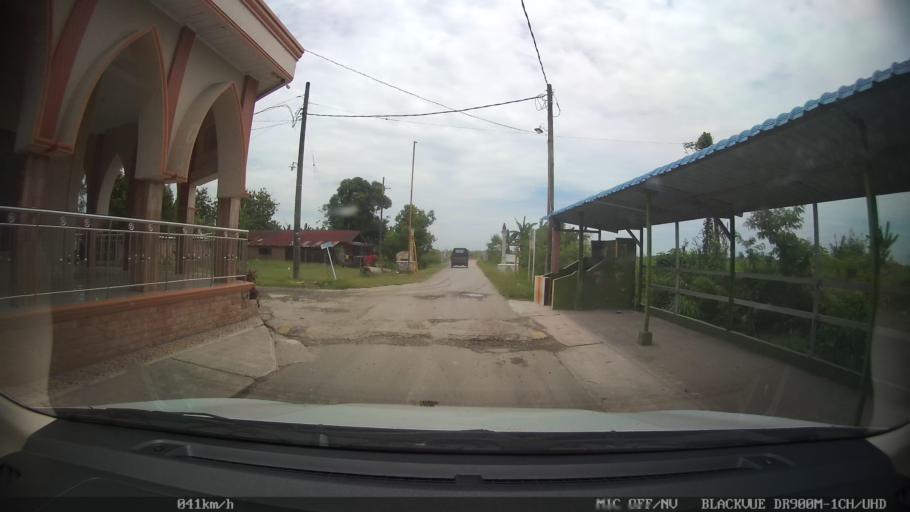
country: ID
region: North Sumatra
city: Sunggal
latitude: 3.6361
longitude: 98.5755
